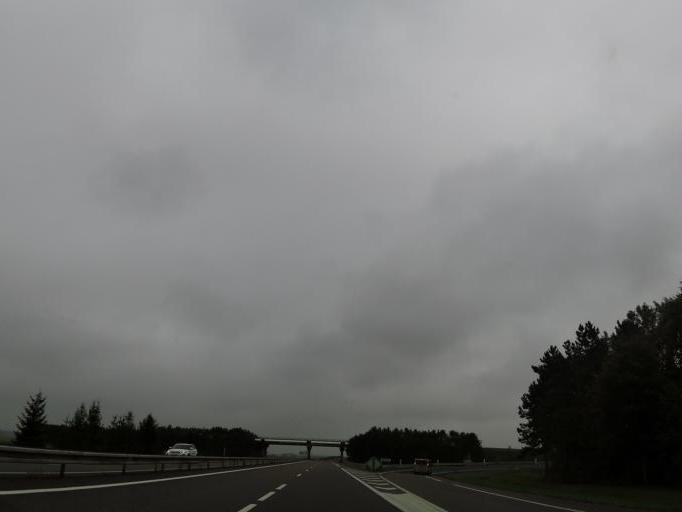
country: FR
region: Champagne-Ardenne
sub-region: Departement de la Marne
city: Courtisols
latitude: 49.0350
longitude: 4.4371
